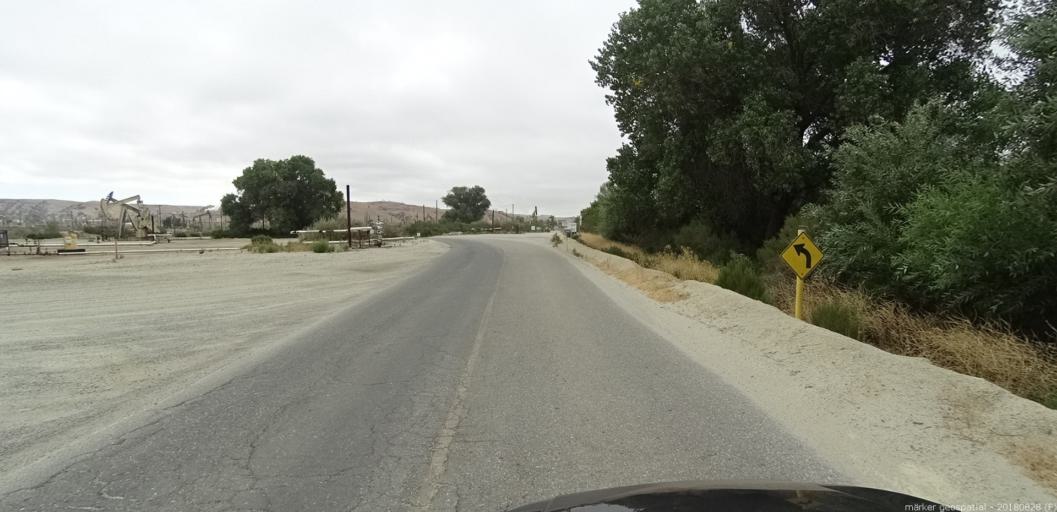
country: US
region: California
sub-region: San Luis Obispo County
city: Lake Nacimiento
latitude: 35.9566
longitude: -120.8764
